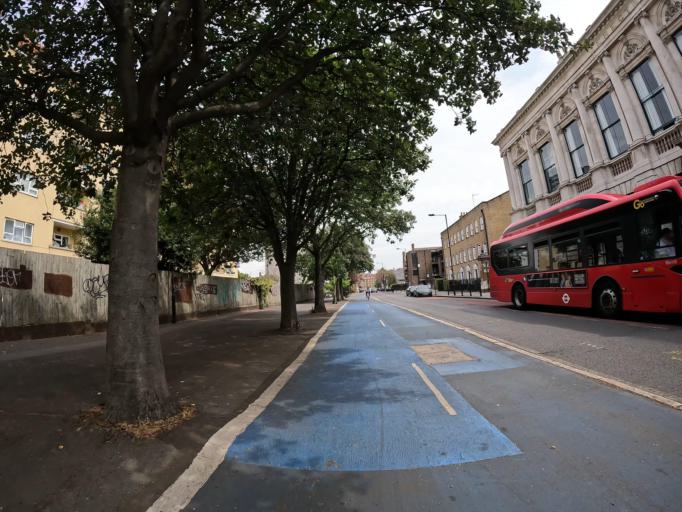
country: GB
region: England
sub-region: Greater London
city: Bethnal Green
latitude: 51.5099
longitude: -0.0594
